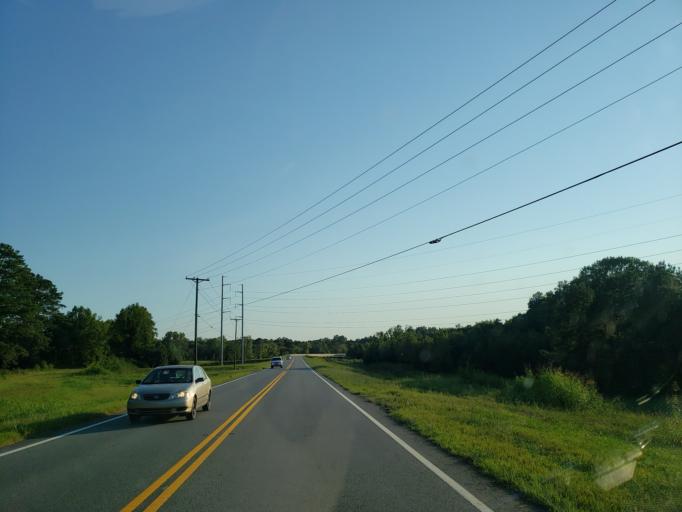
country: US
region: Georgia
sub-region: Gordon County
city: Calhoun
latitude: 34.5458
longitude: -84.8970
